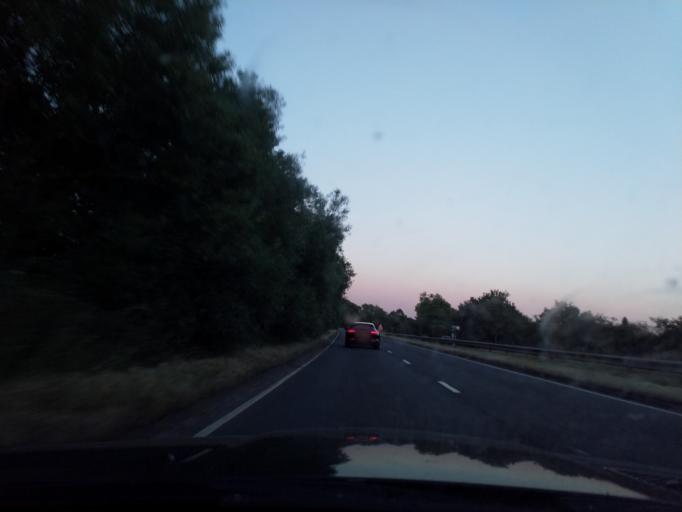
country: GB
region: England
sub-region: Solihull
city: Hampton in Arden
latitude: 52.4382
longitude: -1.6808
